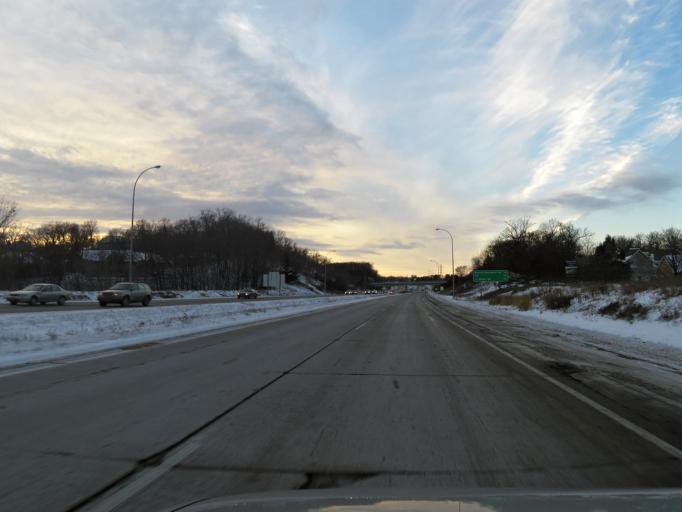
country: US
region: Minnesota
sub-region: Hennepin County
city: Hopkins
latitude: 44.8923
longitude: -93.4281
